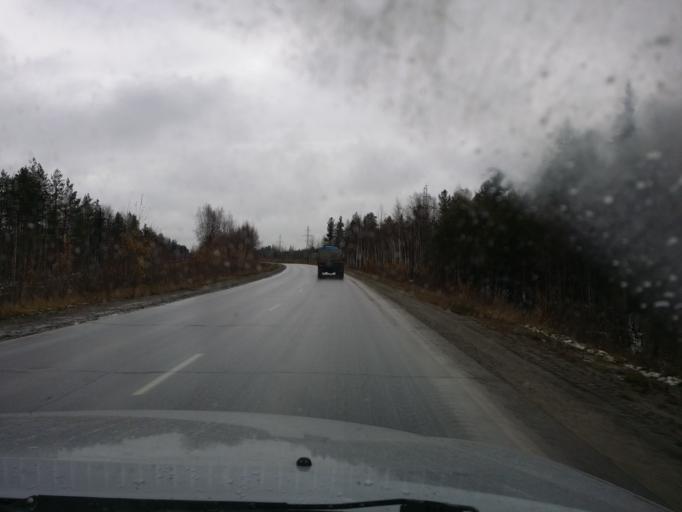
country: RU
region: Khanty-Mansiyskiy Avtonomnyy Okrug
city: Megion
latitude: 61.1426
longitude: 75.7590
